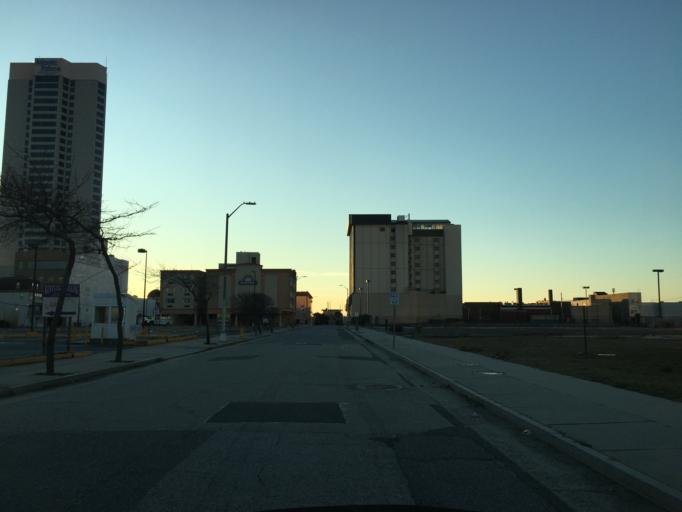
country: US
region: New Jersey
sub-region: Atlantic County
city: Atlantic City
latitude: 39.3586
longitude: -74.4287
